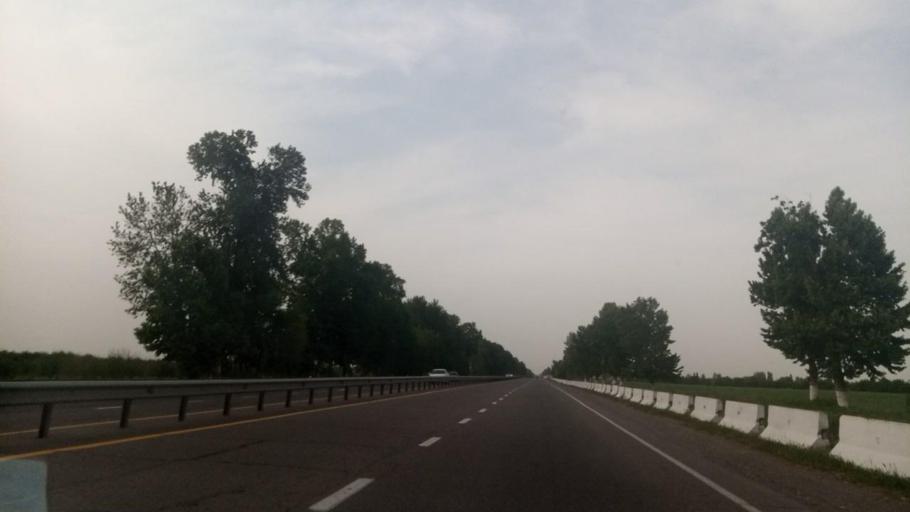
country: UZ
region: Toshkent Shahri
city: Bektemir
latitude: 41.1984
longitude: 69.4031
